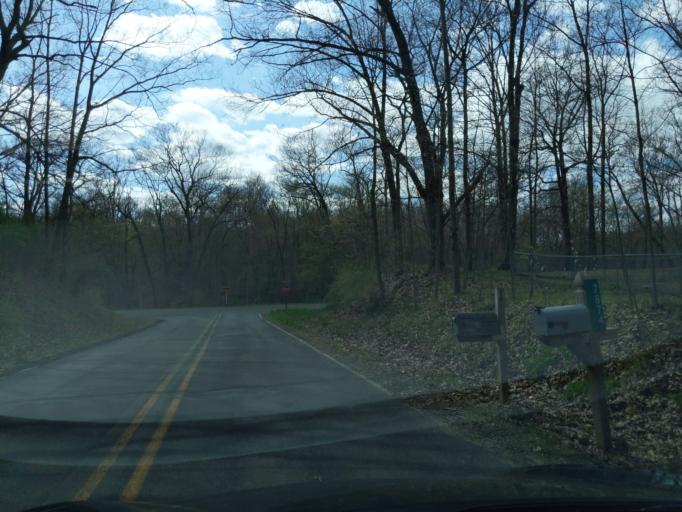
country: US
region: Michigan
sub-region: Ingham County
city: Leslie
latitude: 42.3935
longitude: -84.5408
